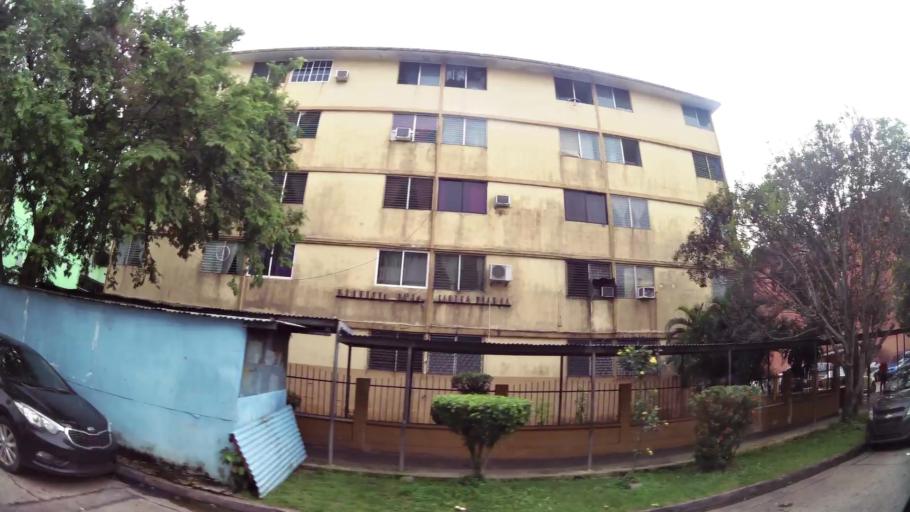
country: PA
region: Panama
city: Panama
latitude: 9.0187
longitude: -79.5313
